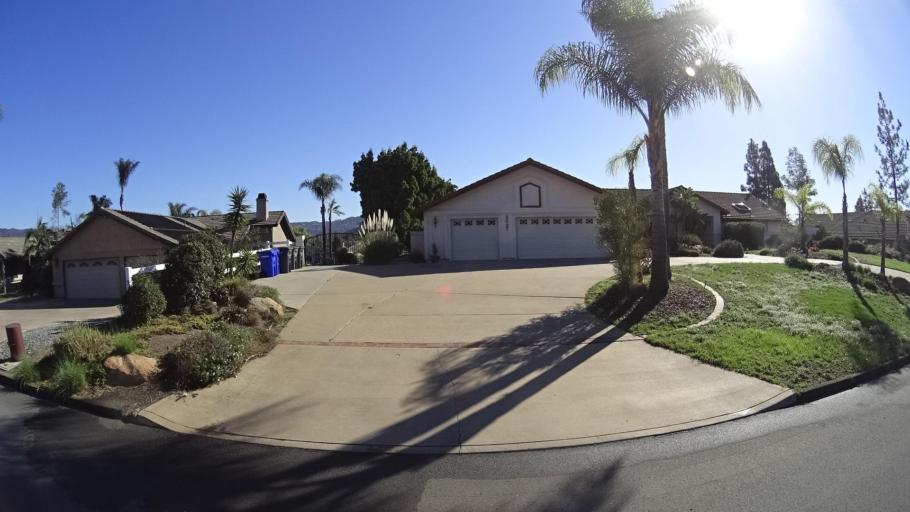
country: US
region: California
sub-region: San Diego County
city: Jamul
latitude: 32.7083
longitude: -116.8764
